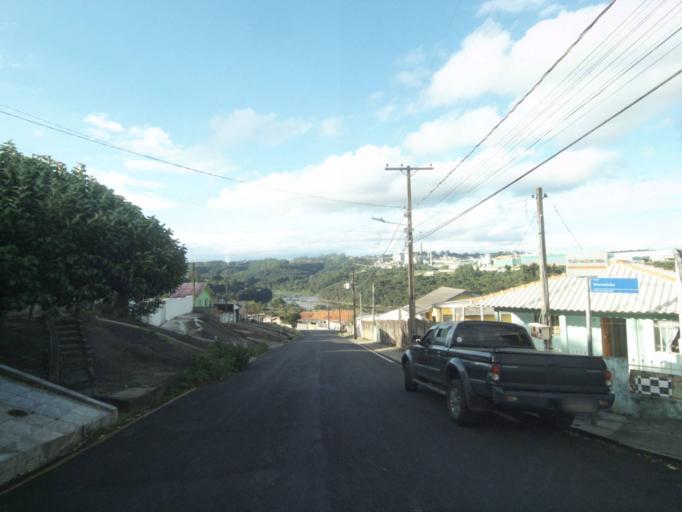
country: BR
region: Parana
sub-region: Telemaco Borba
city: Telemaco Borba
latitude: -24.3250
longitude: -50.6129
